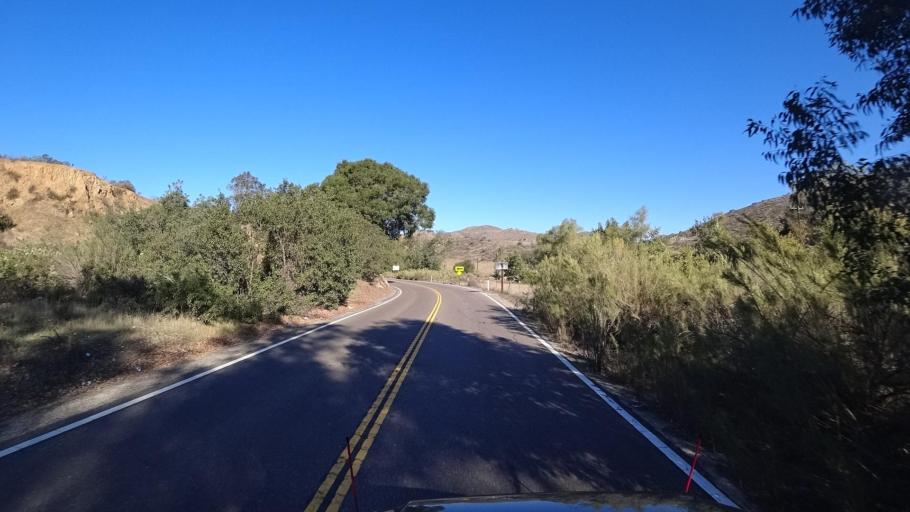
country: US
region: California
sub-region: San Diego County
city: Jamul
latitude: 32.6622
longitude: -116.8126
